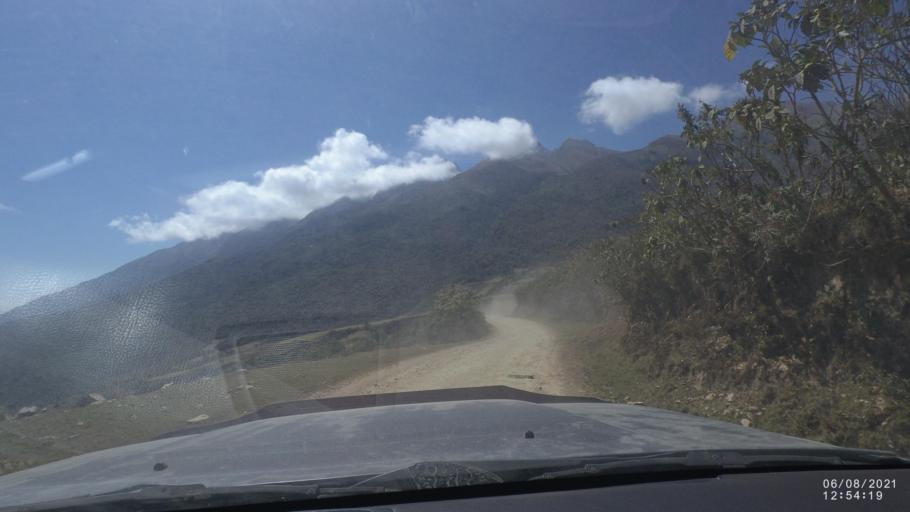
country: BO
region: Cochabamba
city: Colchani
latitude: -16.7585
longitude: -66.6836
